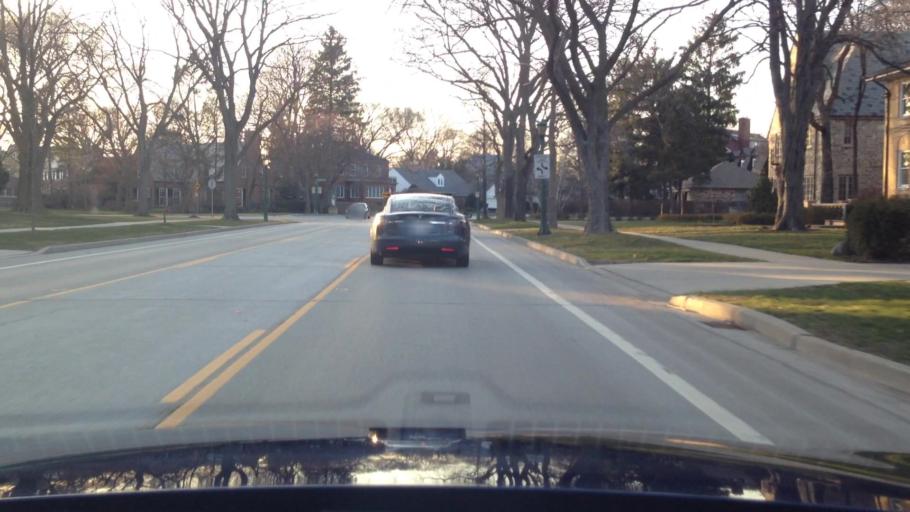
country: US
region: Illinois
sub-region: Cook County
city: Kenilworth
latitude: 42.0822
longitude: -87.6963
